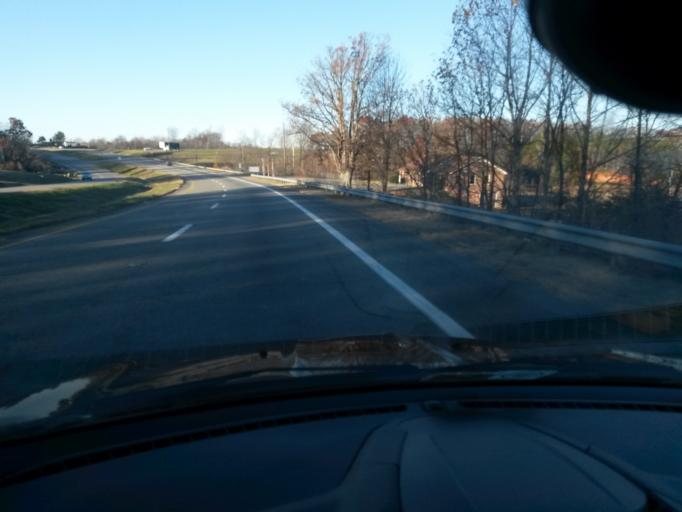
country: US
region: Virginia
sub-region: Henry County
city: Horse Pasture
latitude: 36.6350
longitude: -79.9399
